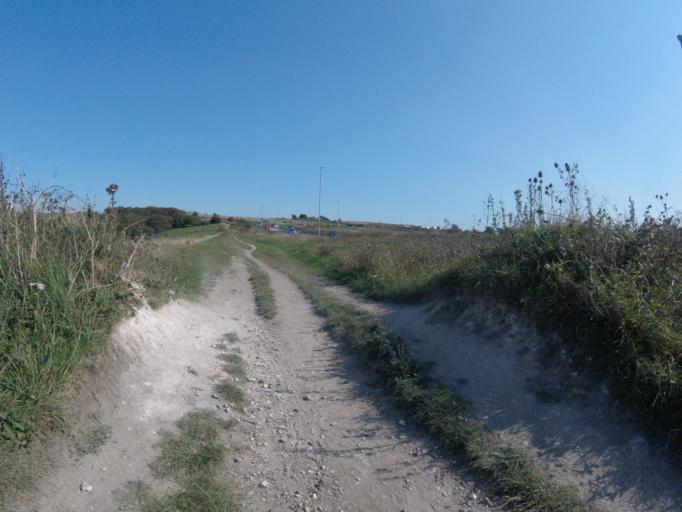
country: GB
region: England
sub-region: Brighton and Hove
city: Brighton
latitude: 50.8356
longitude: -0.1025
